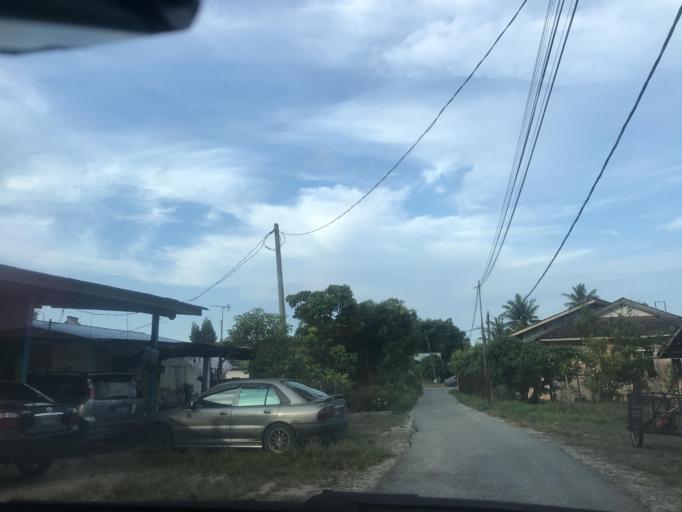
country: MY
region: Kelantan
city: Peringat
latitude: 6.1195
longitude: 102.3565
